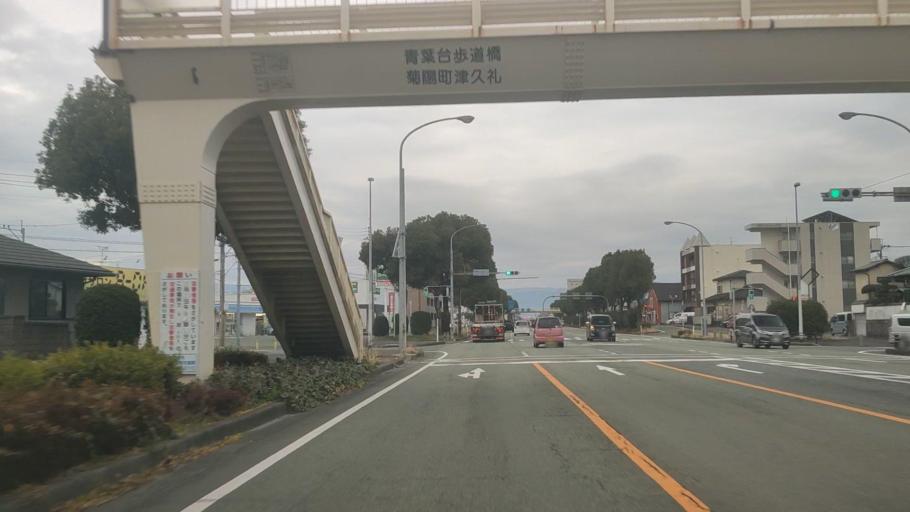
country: JP
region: Kumamoto
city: Ozu
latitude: 32.8582
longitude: 130.7939
